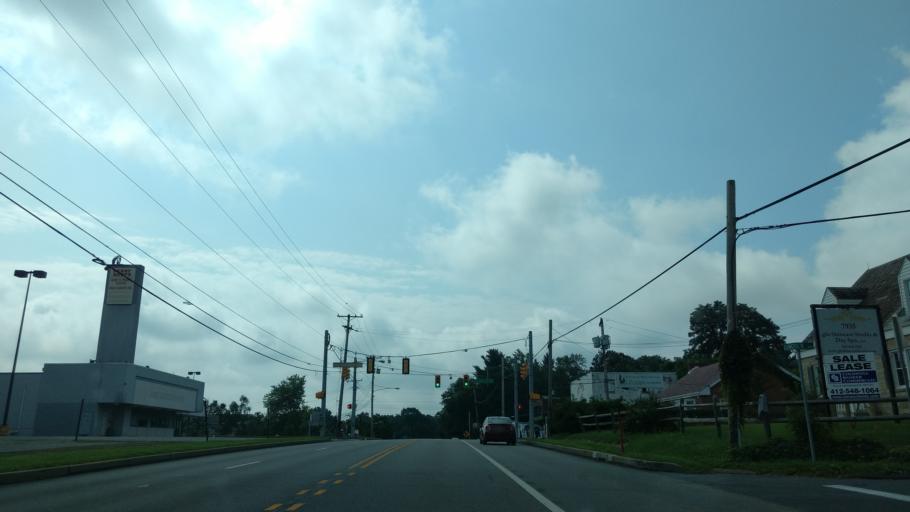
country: US
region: Pennsylvania
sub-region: Allegheny County
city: West View
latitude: 40.5533
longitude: -80.0381
